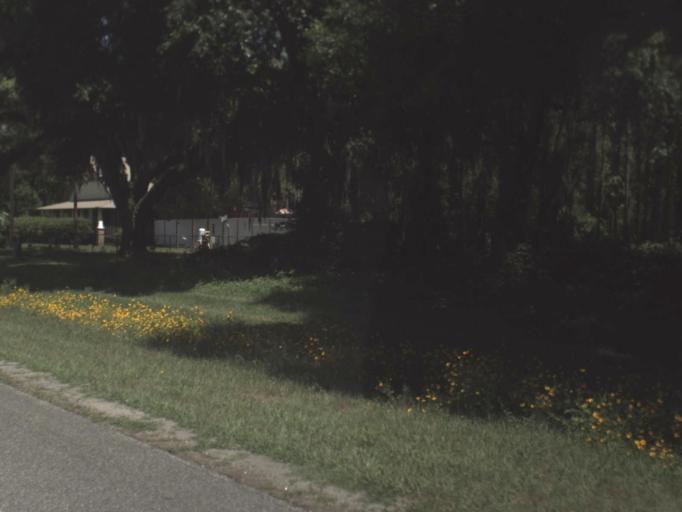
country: US
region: Florida
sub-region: Suwannee County
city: Wellborn
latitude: 30.2561
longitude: -82.9023
